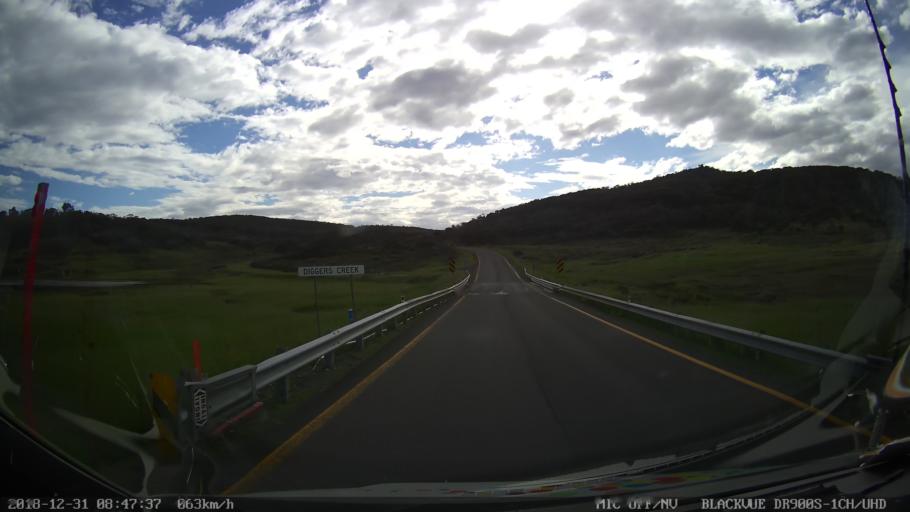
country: AU
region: New South Wales
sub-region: Snowy River
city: Jindabyne
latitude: -36.3605
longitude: 148.4861
